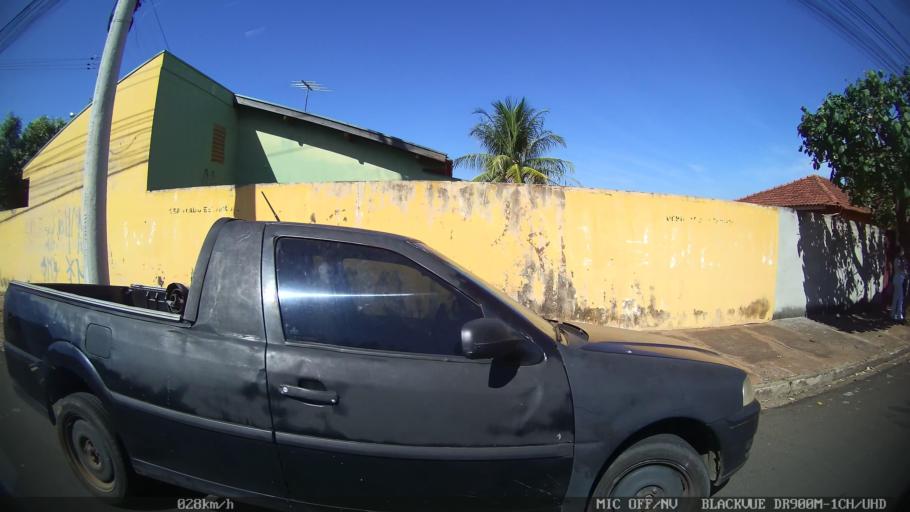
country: BR
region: Sao Paulo
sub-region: Sao Jose Do Rio Preto
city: Sao Jose do Rio Preto
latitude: -20.7714
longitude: -49.4118
